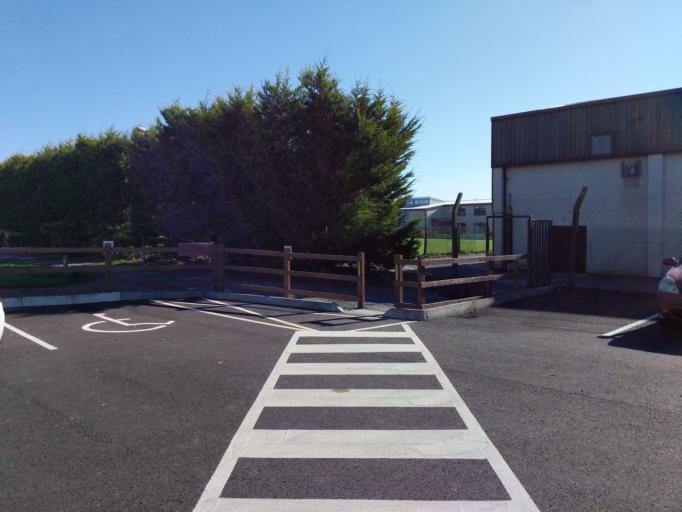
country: IE
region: Munster
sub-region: County Cork
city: Blarney
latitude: 51.9816
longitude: -8.5332
